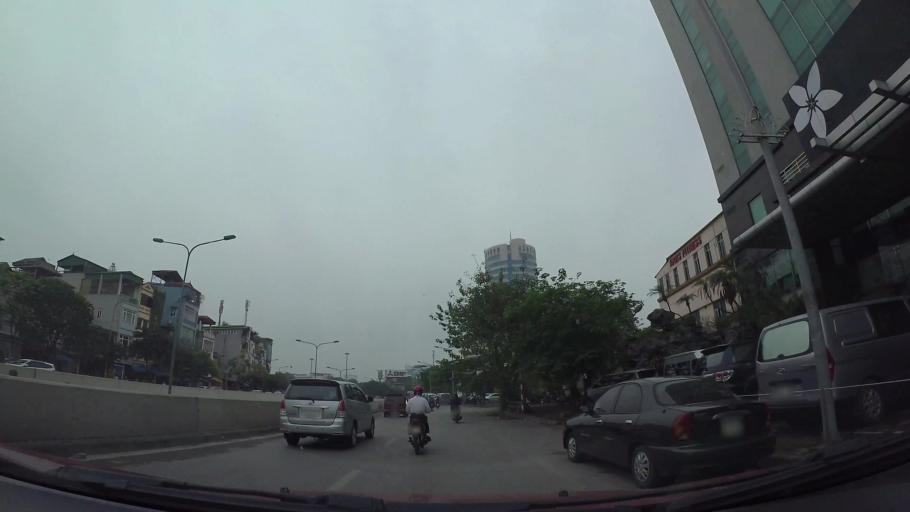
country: VN
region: Ha Noi
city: Hai BaTrung
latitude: 21.0087
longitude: 105.8389
